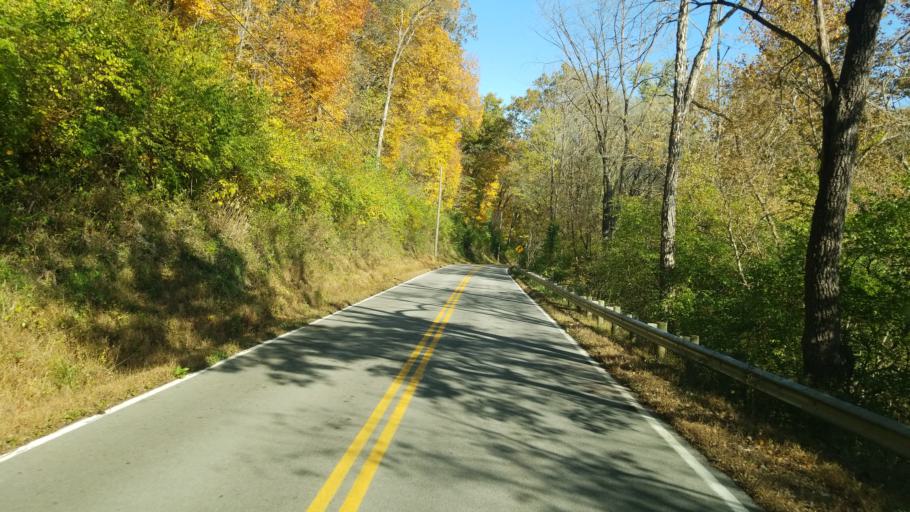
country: US
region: Ohio
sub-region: Warren County
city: Morrow
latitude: 39.3635
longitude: -84.1111
